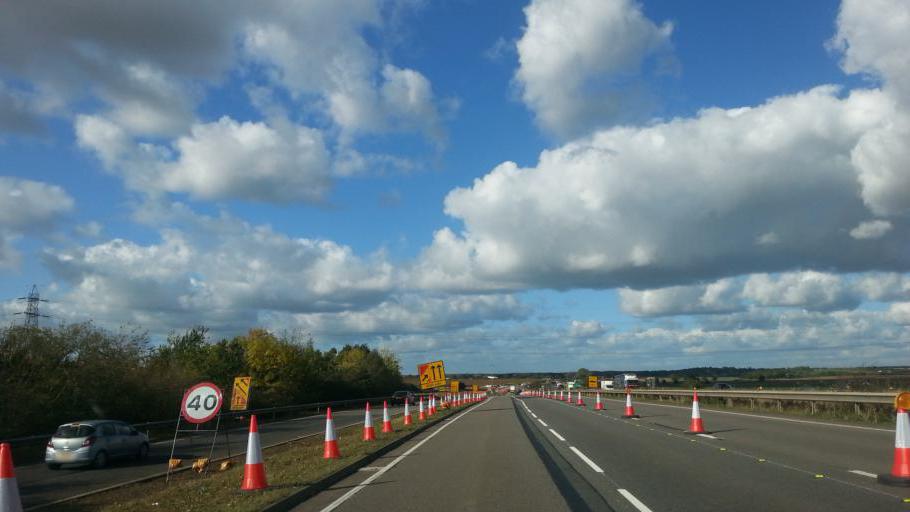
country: GB
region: England
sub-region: Cambridgeshire
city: Brampton
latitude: 52.3350
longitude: -0.2496
